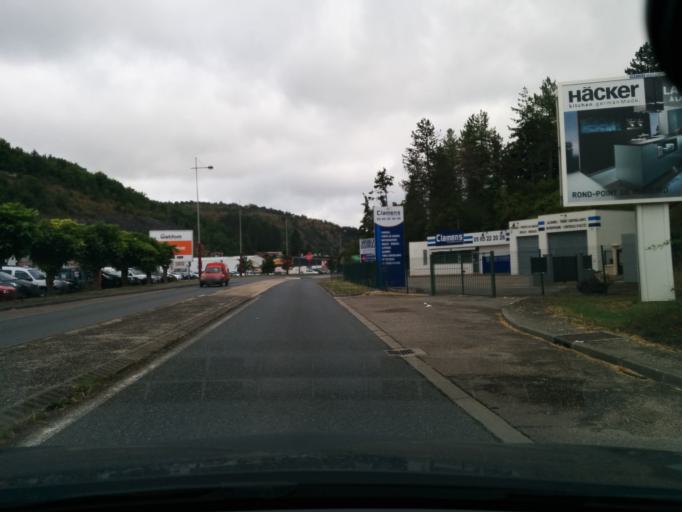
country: FR
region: Midi-Pyrenees
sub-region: Departement du Lot
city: Cahors
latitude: 44.4214
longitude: 1.4393
